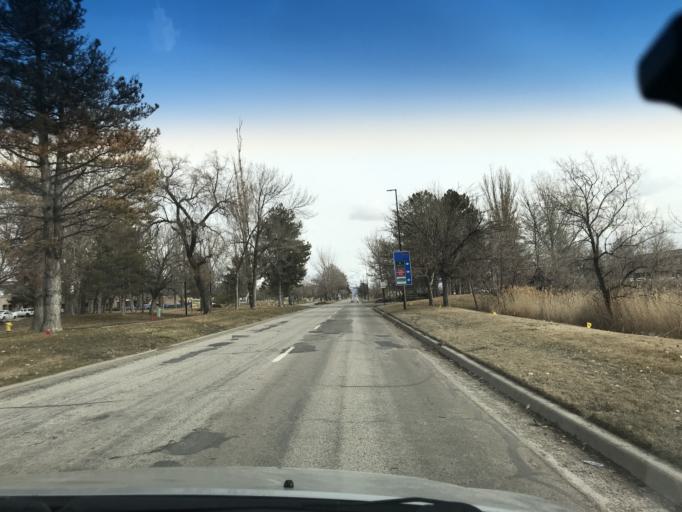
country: US
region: Utah
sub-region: Salt Lake County
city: West Valley City
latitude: 40.7763
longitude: -112.0132
